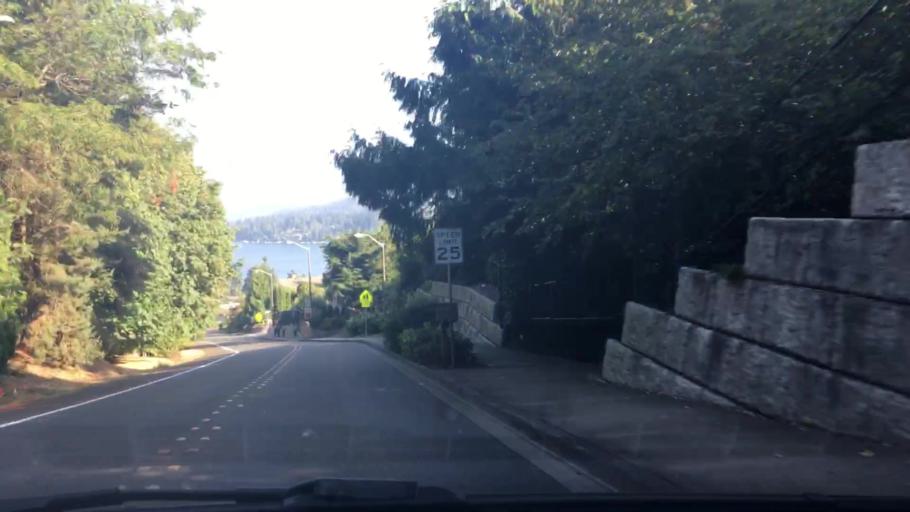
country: US
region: Washington
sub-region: King County
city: West Lake Sammamish
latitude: 47.5887
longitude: -122.1165
